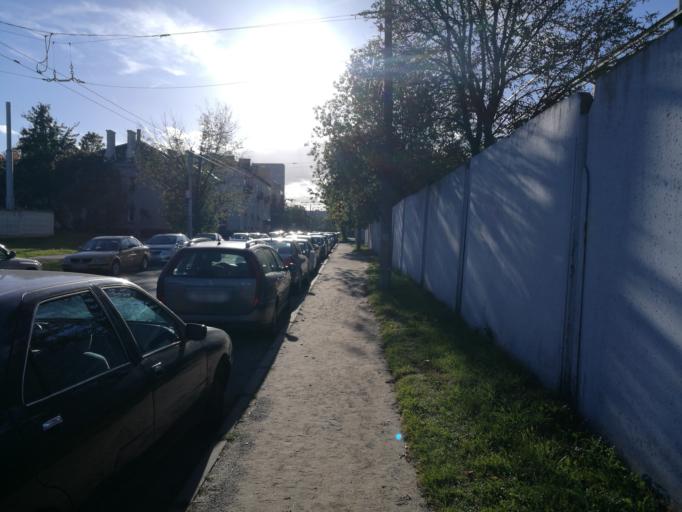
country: BY
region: Minsk
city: Minsk
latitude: 53.9041
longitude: 27.5186
